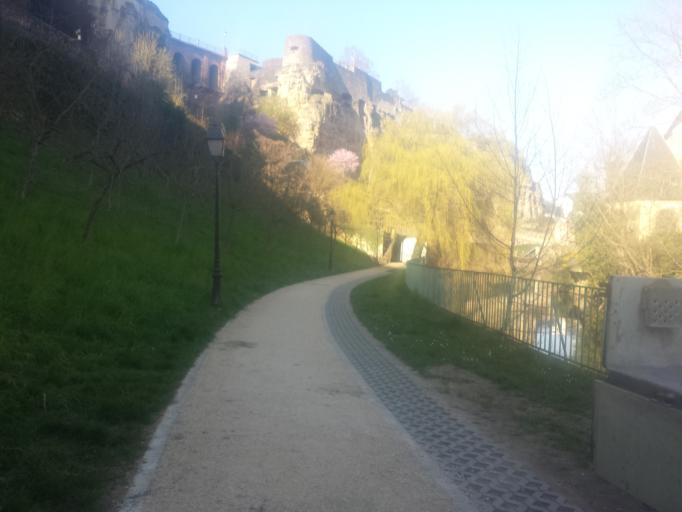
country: LU
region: Luxembourg
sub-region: Canton de Luxembourg
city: Luxembourg
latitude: 49.6105
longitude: 6.1353
